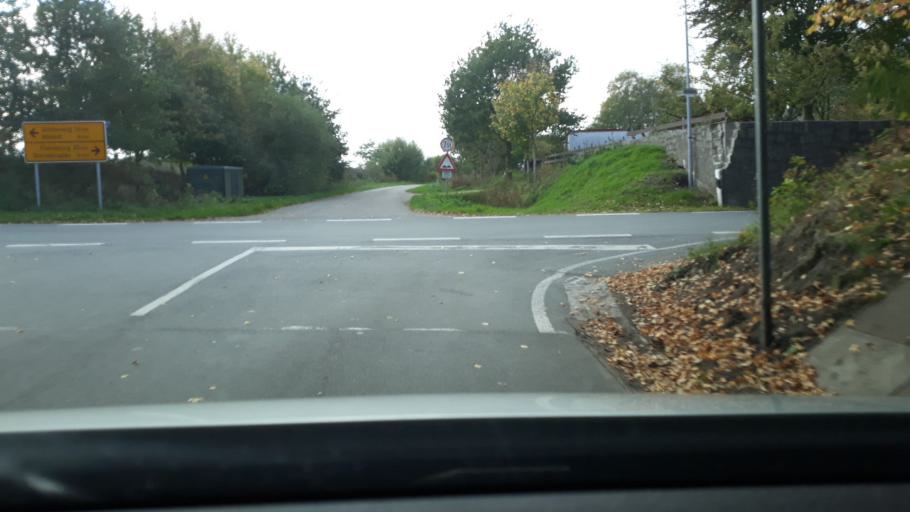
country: DE
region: Schleswig-Holstein
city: Idstedt
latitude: 54.6022
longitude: 9.4796
